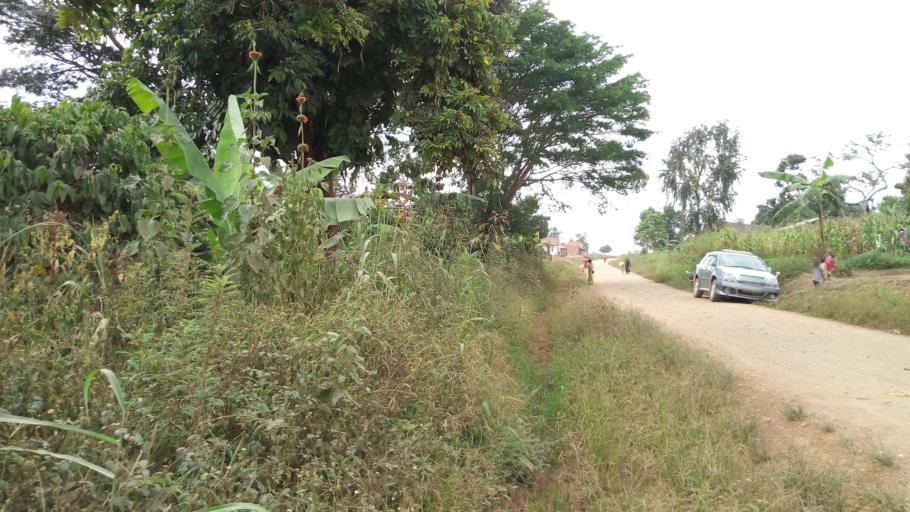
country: UG
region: Central Region
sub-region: Kiboga District
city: Kiboga
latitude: 0.7366
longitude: 31.7271
